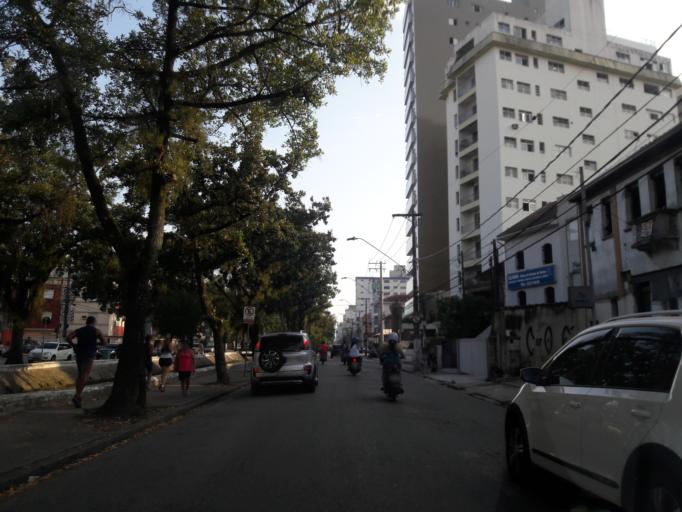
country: BR
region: Sao Paulo
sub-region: Santos
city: Santos
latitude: -23.9540
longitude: -46.3375
